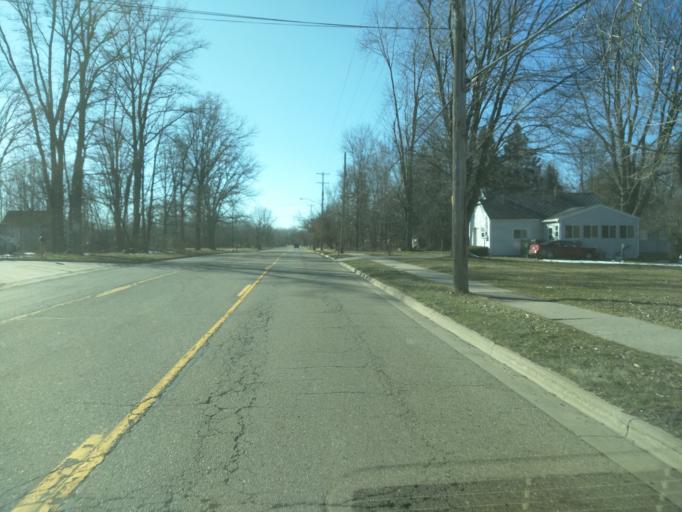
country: US
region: Michigan
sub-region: Eaton County
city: Dimondale
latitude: 42.6693
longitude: -84.5941
